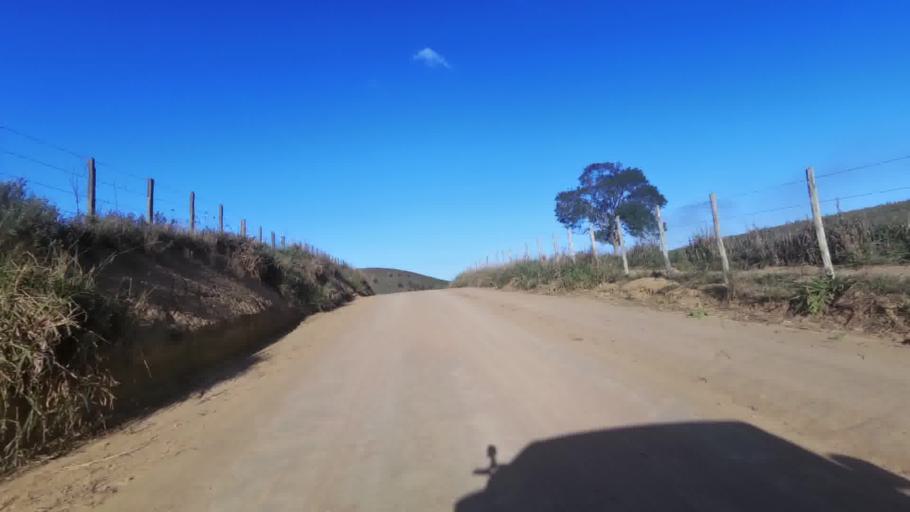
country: BR
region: Espirito Santo
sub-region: Marataizes
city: Marataizes
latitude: -21.1321
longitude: -41.0127
